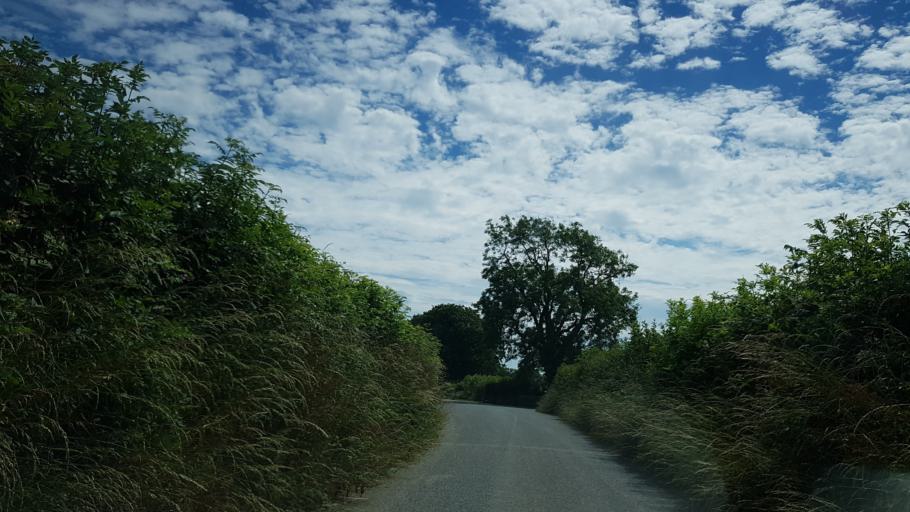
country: GB
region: Wales
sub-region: Pembrokeshire
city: Wiston
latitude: 51.8217
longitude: -4.9187
